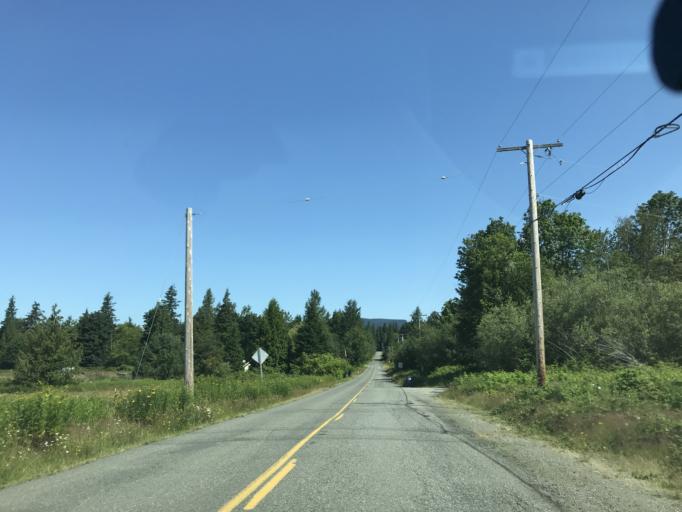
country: US
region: Washington
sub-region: King County
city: Ravensdale
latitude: 47.3635
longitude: -121.8802
